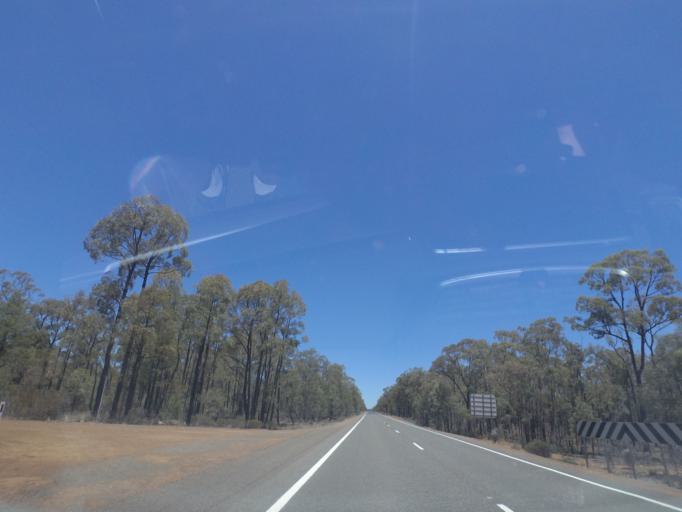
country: AU
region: New South Wales
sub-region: Warrumbungle Shire
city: Coonabarabran
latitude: -30.8582
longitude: 149.4552
